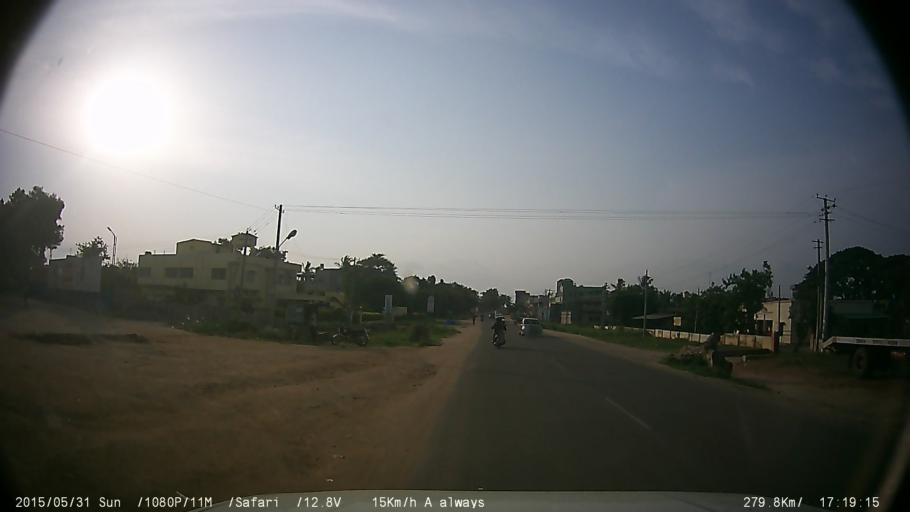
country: IN
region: Karnataka
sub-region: Chamrajnagar
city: Gundlupet
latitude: 11.8149
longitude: 76.6856
